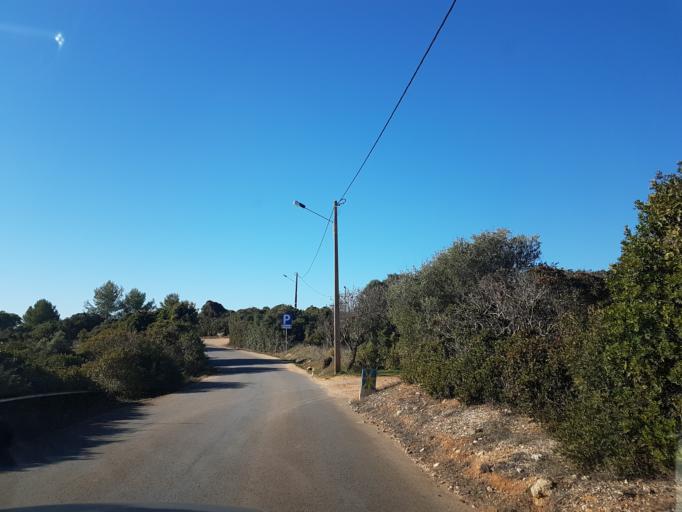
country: PT
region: Faro
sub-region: Lagoa
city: Carvoeiro
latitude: 37.0900
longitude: -8.4227
